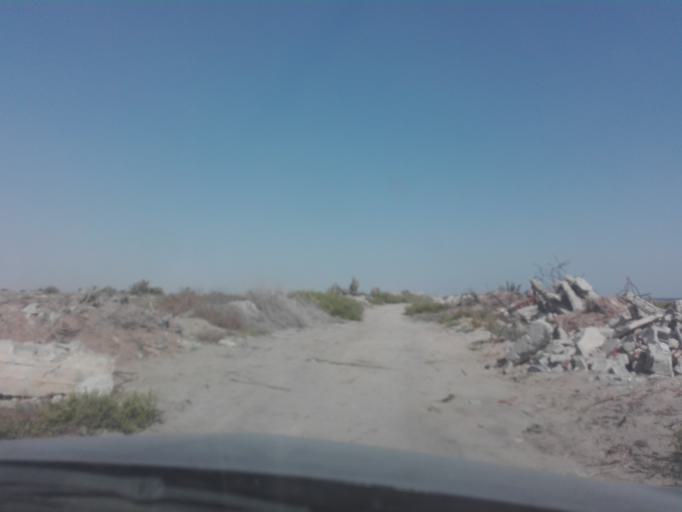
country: TN
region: Qabis
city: Gabes
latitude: 33.9667
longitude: 10.0638
